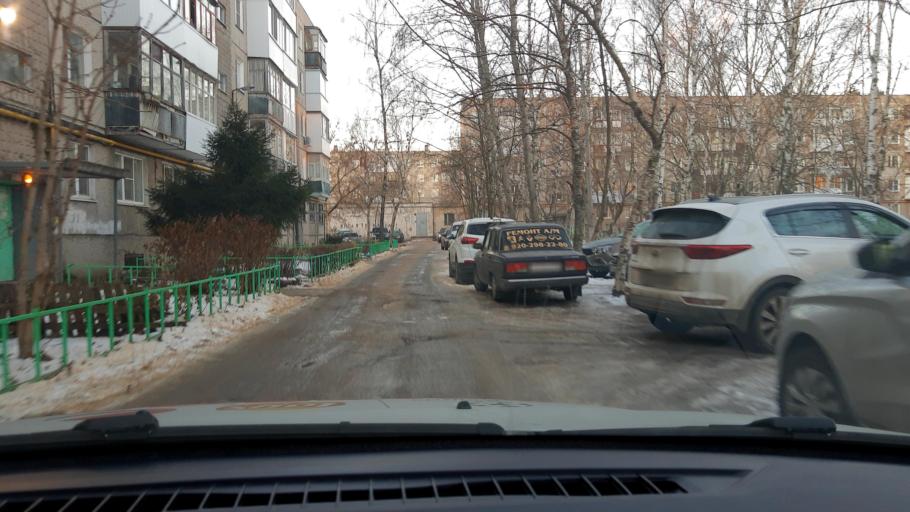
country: RU
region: Nizjnij Novgorod
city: Dzerzhinsk
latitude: 56.2339
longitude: 43.4013
